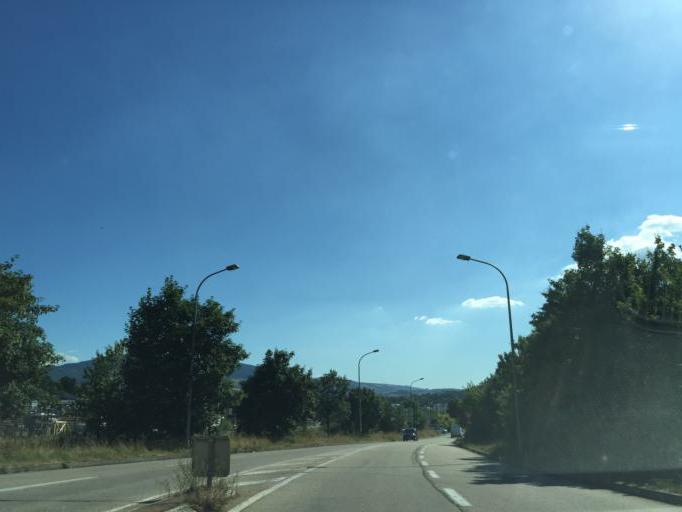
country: FR
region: Rhone-Alpes
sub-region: Departement de la Loire
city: Saint-Chamond
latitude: 45.4931
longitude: 4.5268
